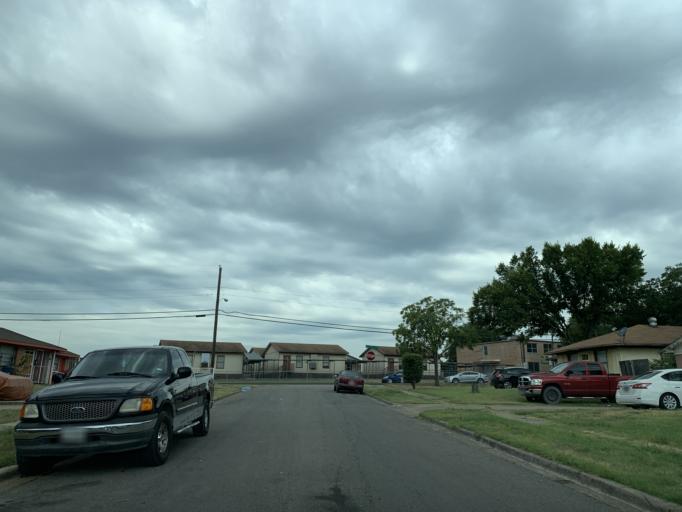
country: US
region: Texas
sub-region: Dallas County
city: DeSoto
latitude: 32.6647
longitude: -96.8291
